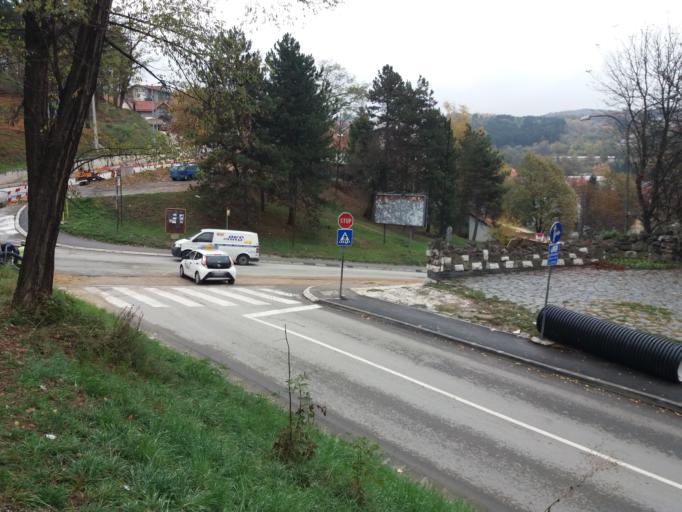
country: RS
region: Central Serbia
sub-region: Zlatiborski Okrug
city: Uzice
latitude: 43.8515
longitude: 19.8507
